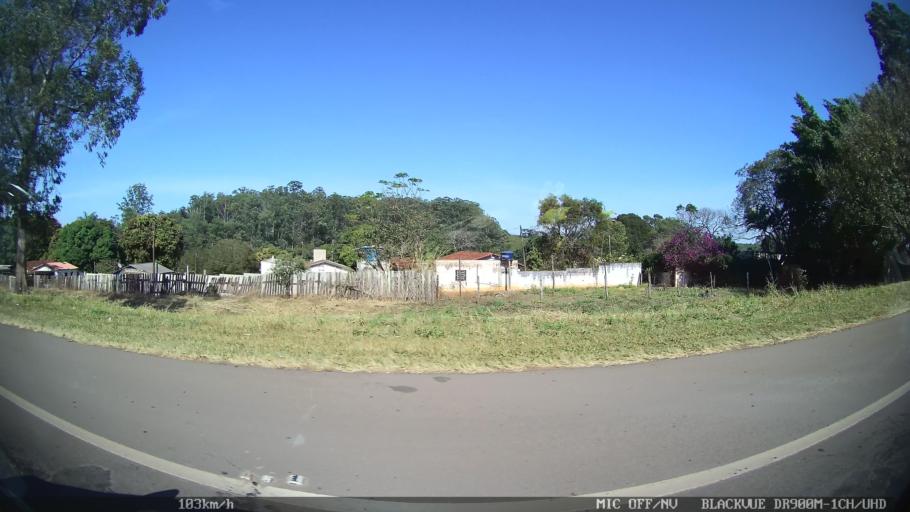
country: BR
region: Sao Paulo
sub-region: Batatais
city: Batatais
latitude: -20.9076
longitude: -47.5959
